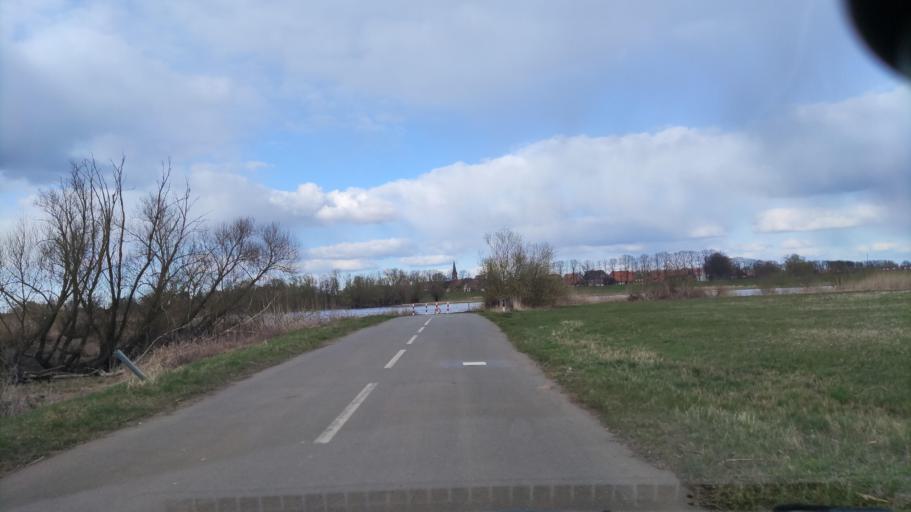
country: DE
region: Mecklenburg-Vorpommern
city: Domitz
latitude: 53.1364
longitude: 11.2413
